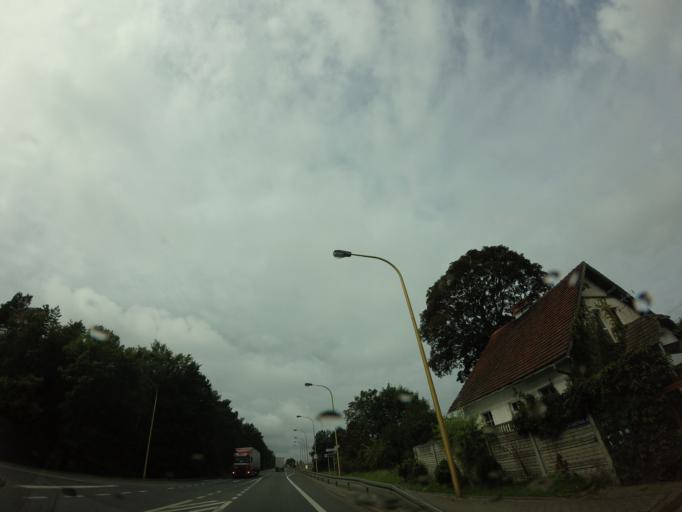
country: PL
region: West Pomeranian Voivodeship
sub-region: Swinoujscie
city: Swinoujscie
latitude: 53.8972
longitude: 14.3353
